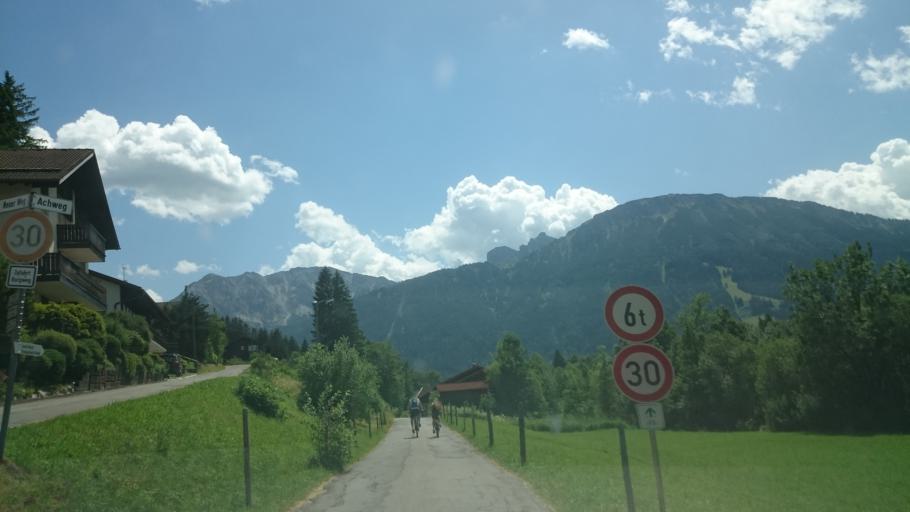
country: DE
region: Bavaria
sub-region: Swabia
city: Pfronten
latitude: 47.5817
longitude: 10.5683
